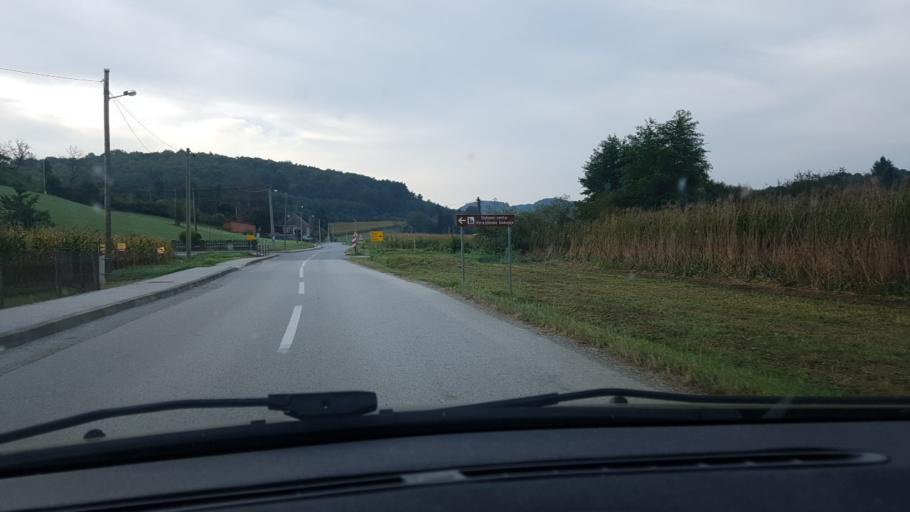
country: HR
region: Krapinsko-Zagorska
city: Mihovljan
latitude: 46.1457
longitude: 15.9622
